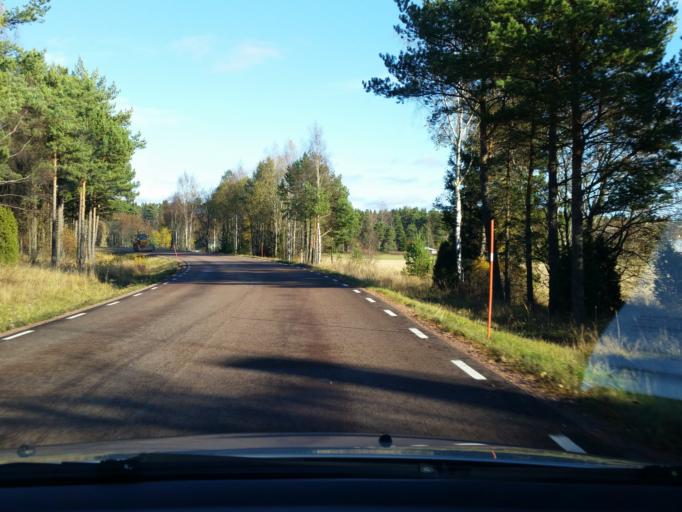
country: AX
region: Mariehamns stad
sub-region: Mariehamn
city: Mariehamn
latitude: 60.1329
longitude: 19.8502
